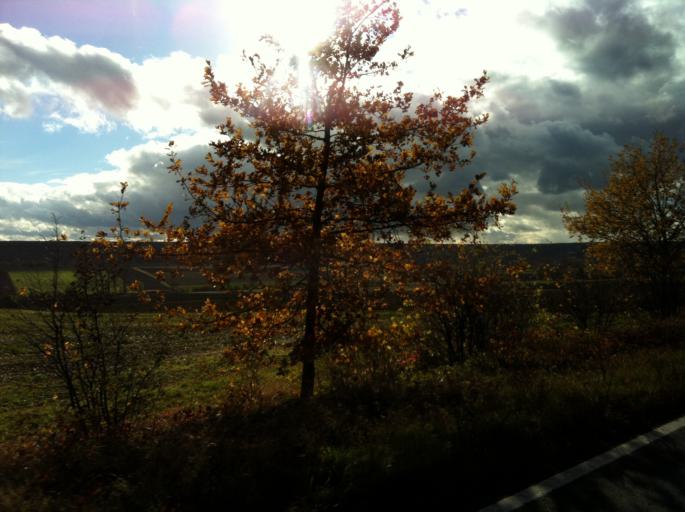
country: DE
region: Rheinland-Pfalz
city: Stadecken-Elsheim
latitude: 49.9037
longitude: 8.1089
